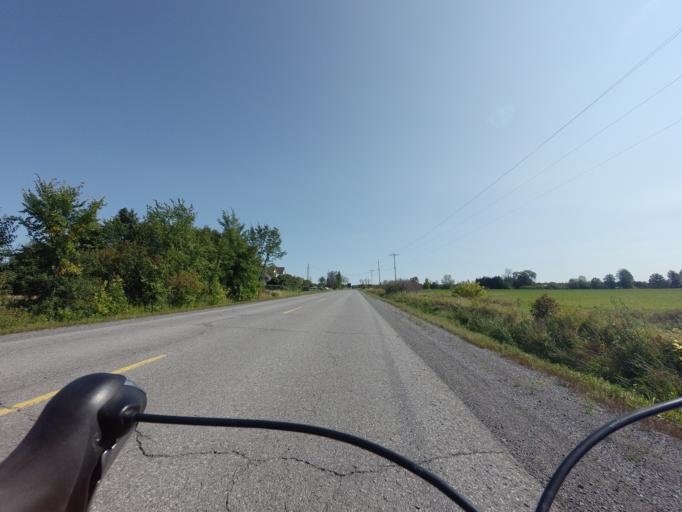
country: CA
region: Ontario
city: Carleton Place
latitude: 45.3362
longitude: -76.0954
